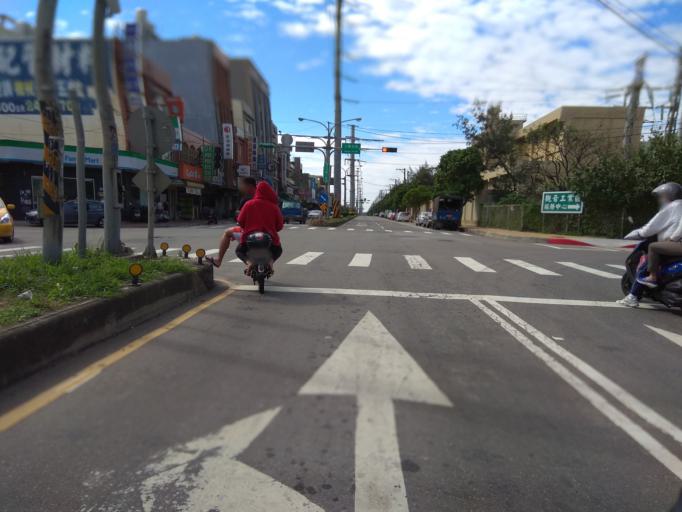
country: TW
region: Taiwan
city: Taoyuan City
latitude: 25.0519
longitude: 121.1182
